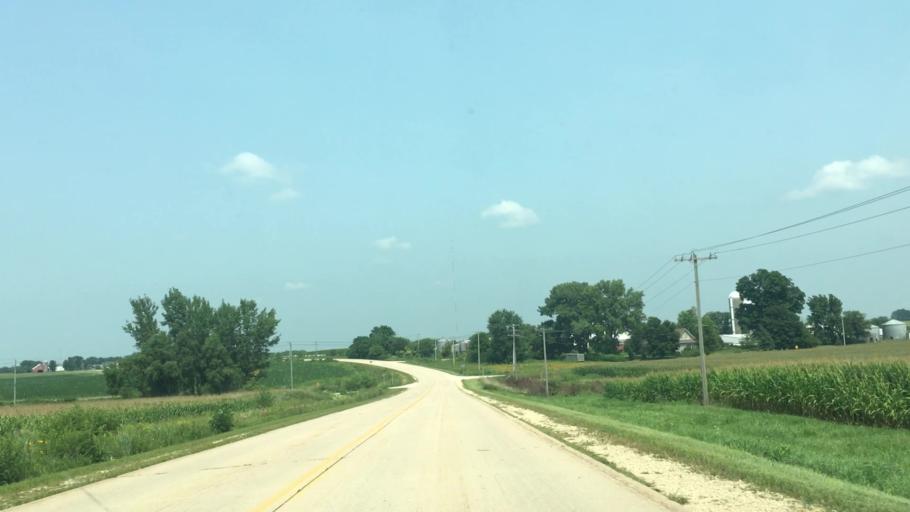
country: US
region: Iowa
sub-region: Fayette County
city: Oelwein
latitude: 42.6631
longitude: -91.8958
